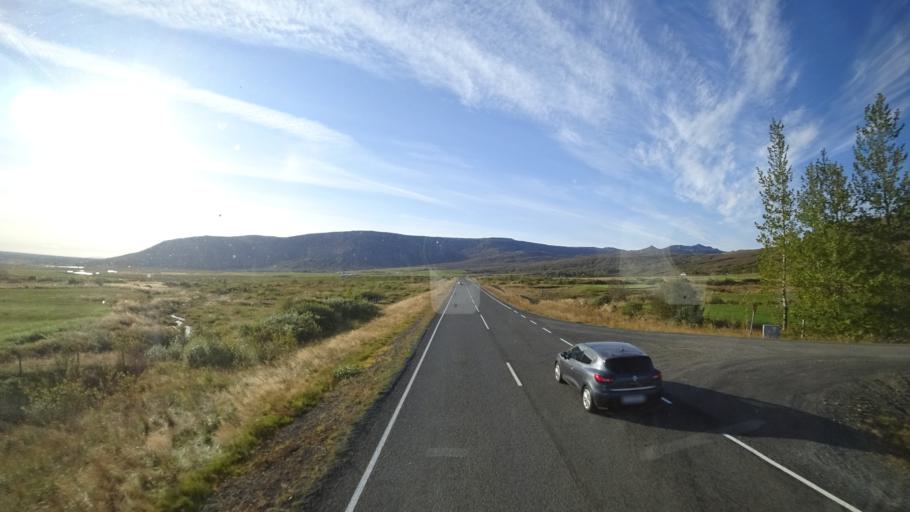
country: IS
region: South
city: Selfoss
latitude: 64.2369
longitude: -20.6479
